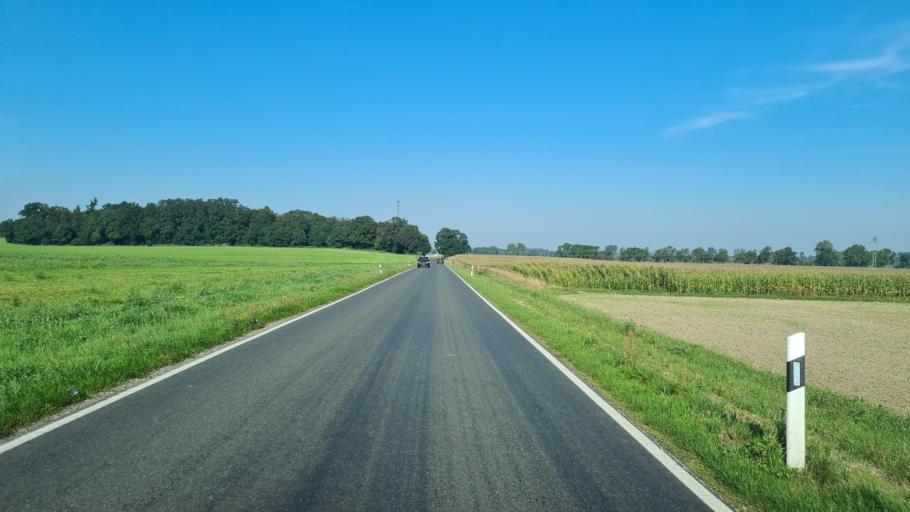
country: DE
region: Brandenburg
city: Friesack
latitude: 52.7346
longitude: 12.6031
